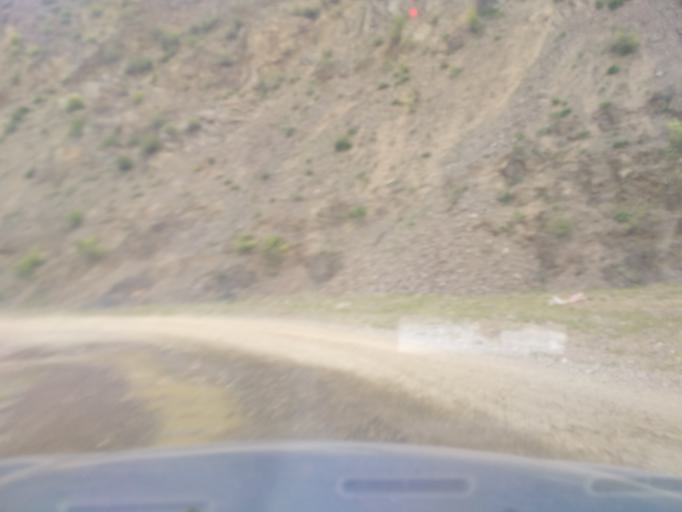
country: UZ
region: Jizzax
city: Zomin
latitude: 39.8543
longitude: 68.3922
